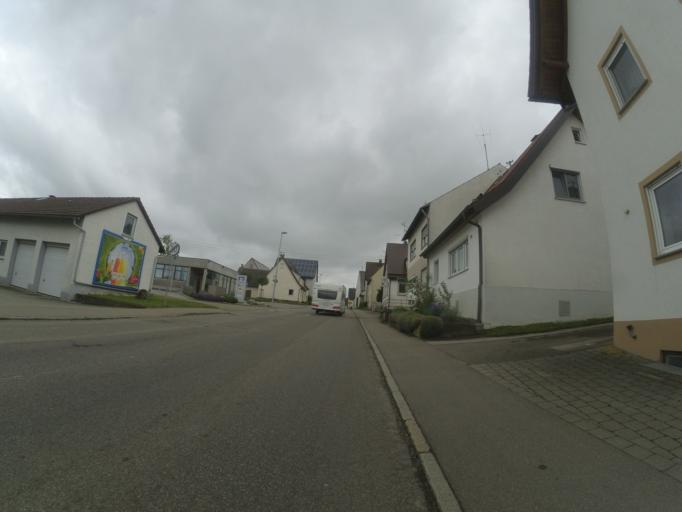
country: DE
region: Baden-Wuerttemberg
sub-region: Tuebingen Region
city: Bernstadt
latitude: 48.4997
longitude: 10.0248
